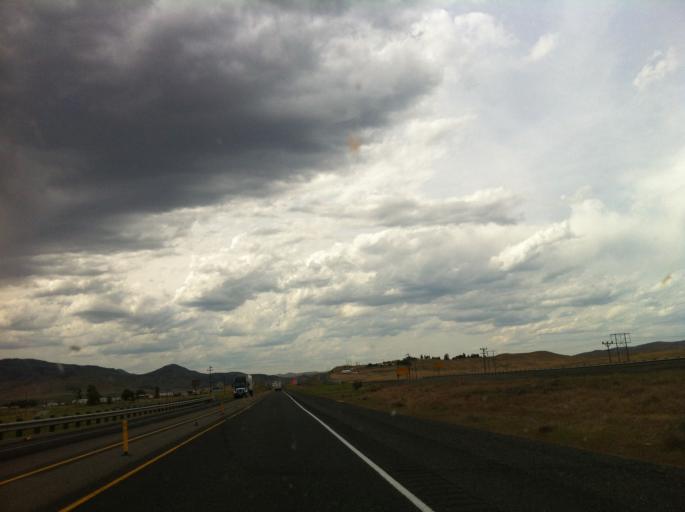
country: US
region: Oregon
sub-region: Baker County
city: Baker City
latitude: 44.5602
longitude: -117.4286
